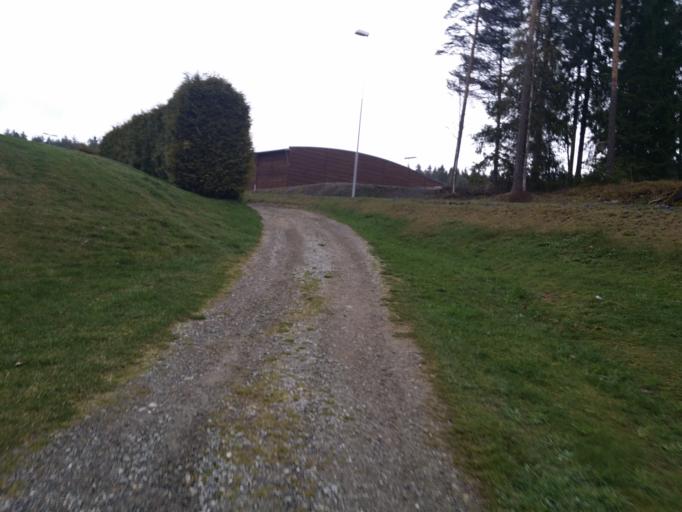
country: NO
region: Akershus
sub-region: Oppegard
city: Kolbotn
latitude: 59.7731
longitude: 10.8138
